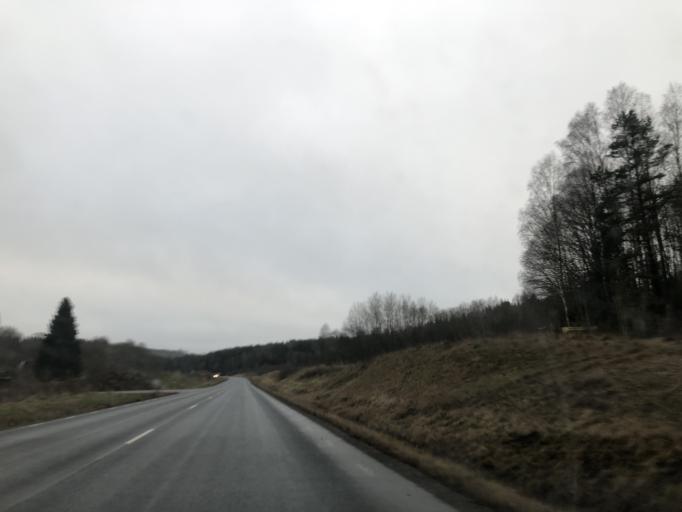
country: SE
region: Vaestra Goetaland
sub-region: Ulricehamns Kommun
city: Ulricehamn
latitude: 57.8263
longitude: 13.2890
